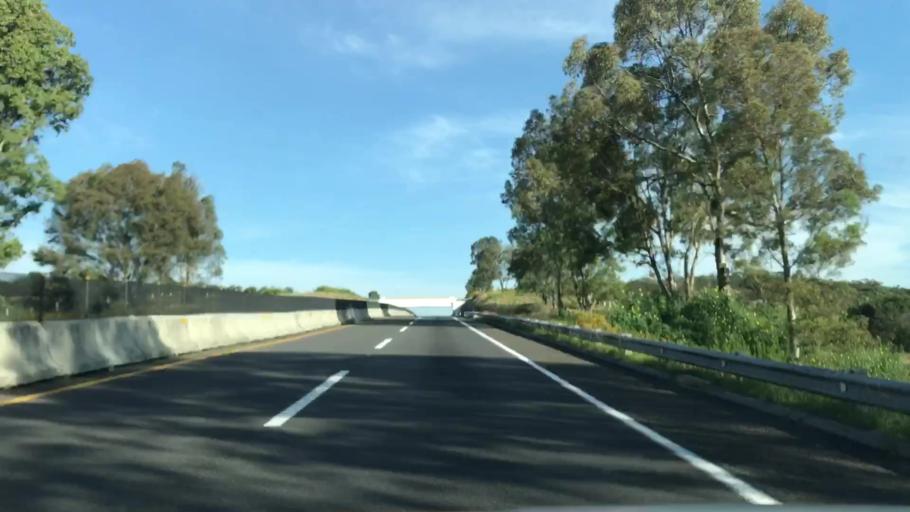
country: MX
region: Jalisco
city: Encarnacion de Diaz
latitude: 21.3819
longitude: -102.1395
